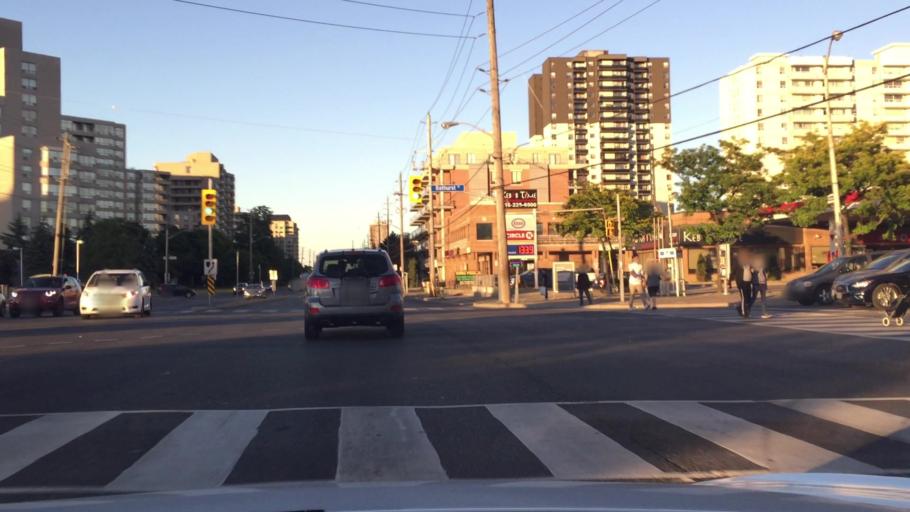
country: CA
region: Ontario
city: Concord
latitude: 43.7923
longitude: -79.4459
